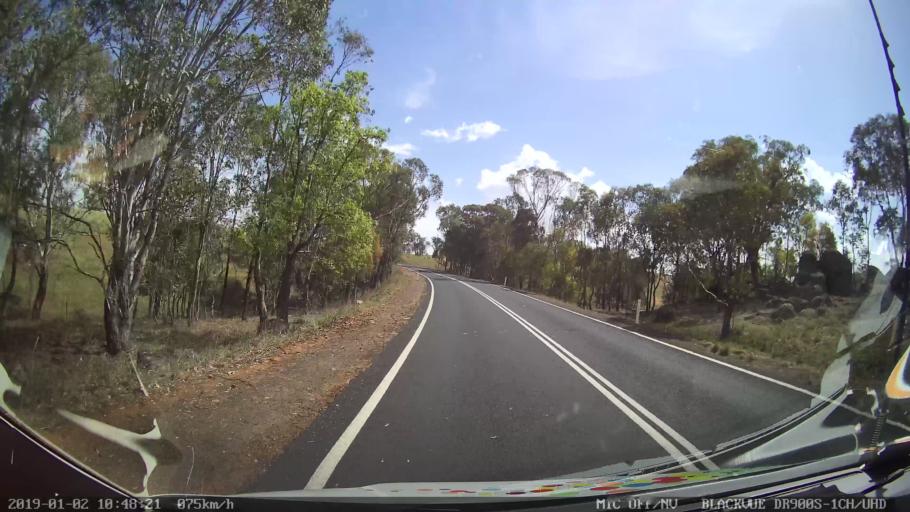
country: AU
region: New South Wales
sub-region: Cootamundra
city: Cootamundra
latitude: -34.7376
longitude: 148.2778
